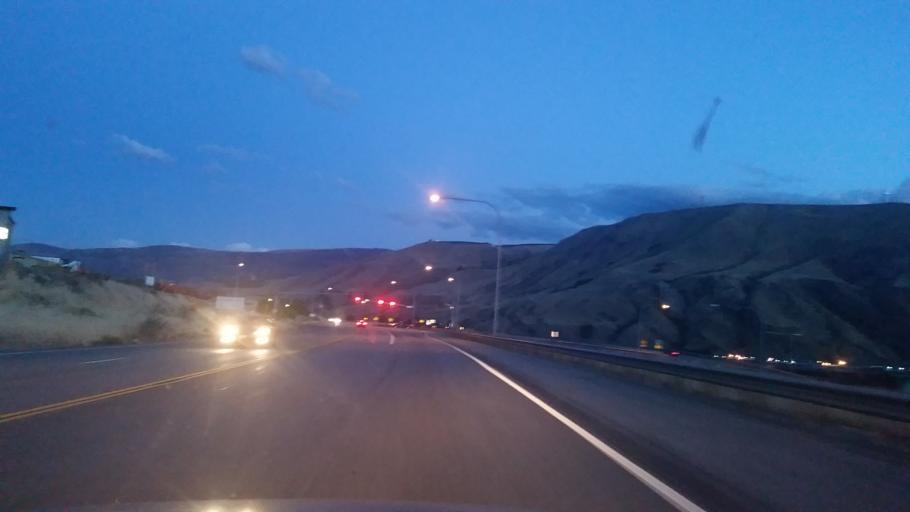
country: US
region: Washington
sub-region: Chelan County
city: South Wenatchee
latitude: 47.4009
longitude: -120.2884
